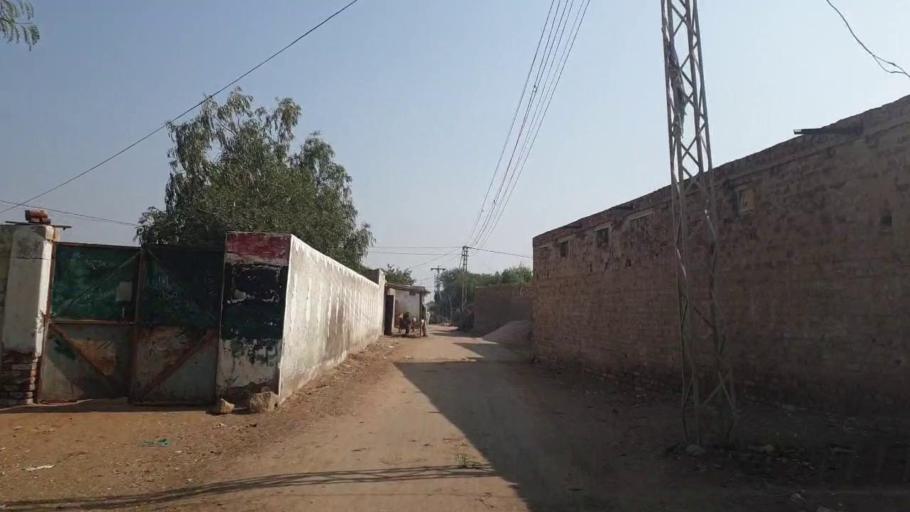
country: PK
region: Sindh
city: Jamshoro
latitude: 25.4805
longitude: 68.2829
